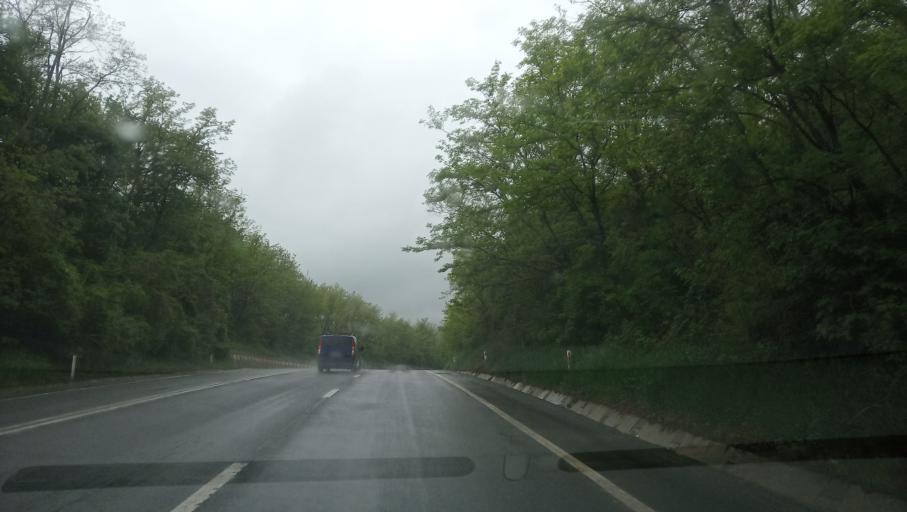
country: RO
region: Sibiu
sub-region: Comuna Orlat
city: Orlat
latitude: 45.7784
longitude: 23.9630
